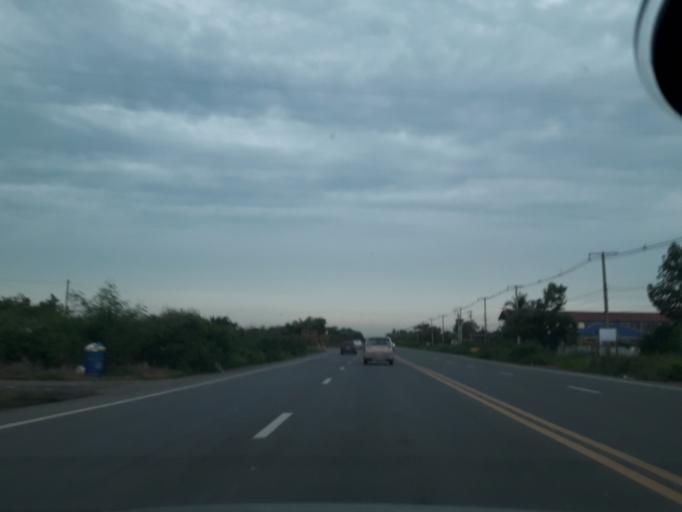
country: TH
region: Pathum Thani
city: Ban Rangsit
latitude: 14.0810
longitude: 100.7472
